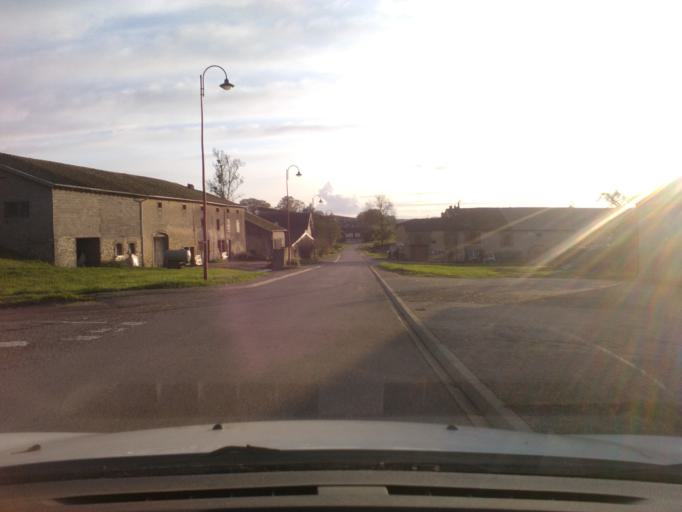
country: FR
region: Lorraine
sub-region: Departement des Vosges
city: Mirecourt
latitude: 48.2500
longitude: 6.1570
